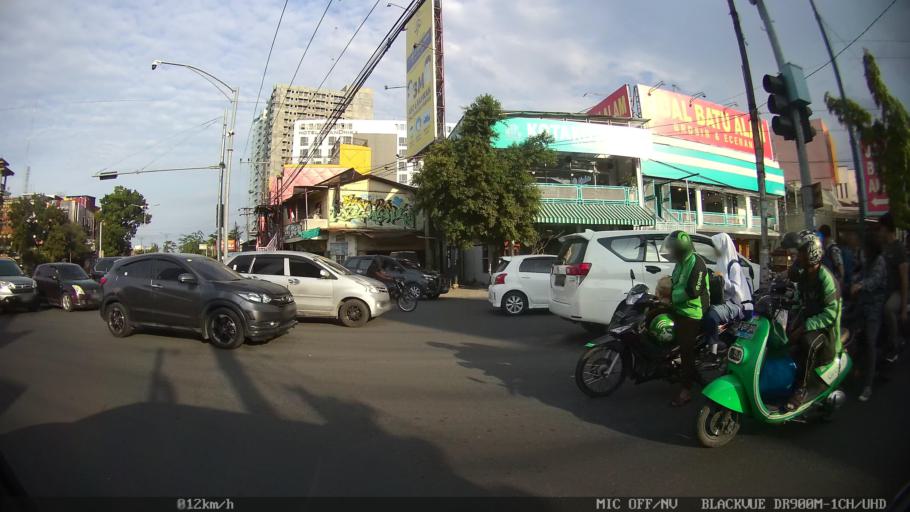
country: ID
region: North Sumatra
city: Sunggal
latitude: 3.5672
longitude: 98.6418
